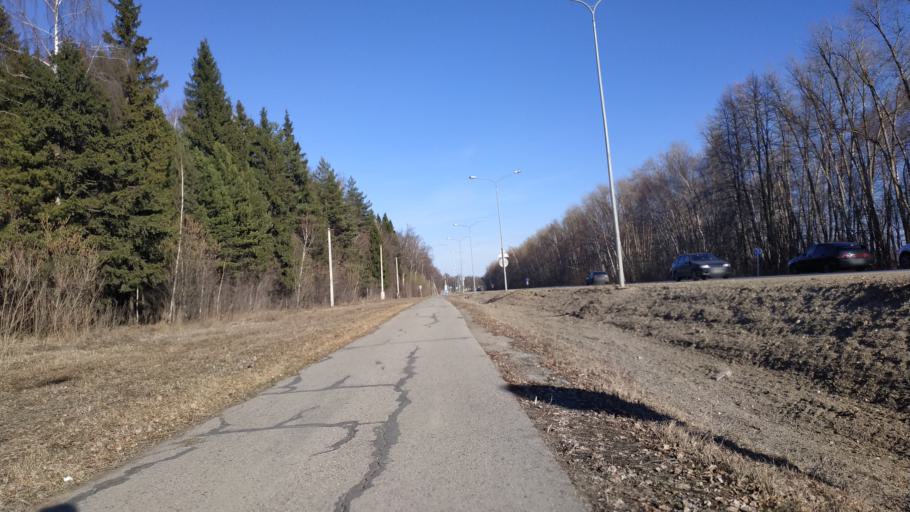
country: RU
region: Chuvashia
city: Ishley
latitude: 56.1347
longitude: 47.0981
